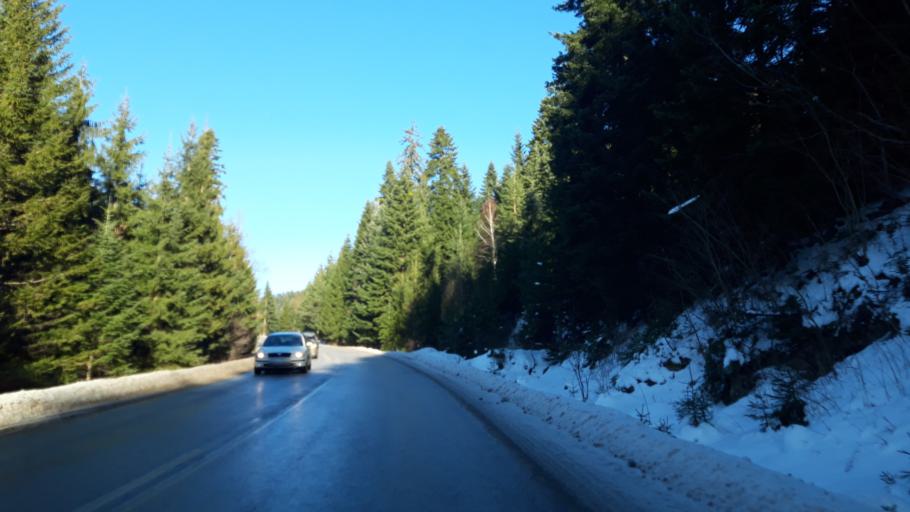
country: BA
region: Republika Srpska
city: Pale
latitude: 43.9131
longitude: 18.6449
